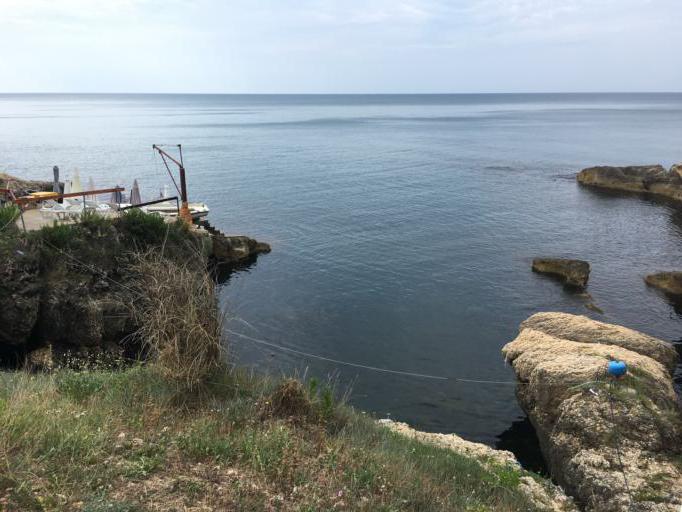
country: ME
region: Ulcinj
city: Ulcinj
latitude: 41.9171
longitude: 19.2203
